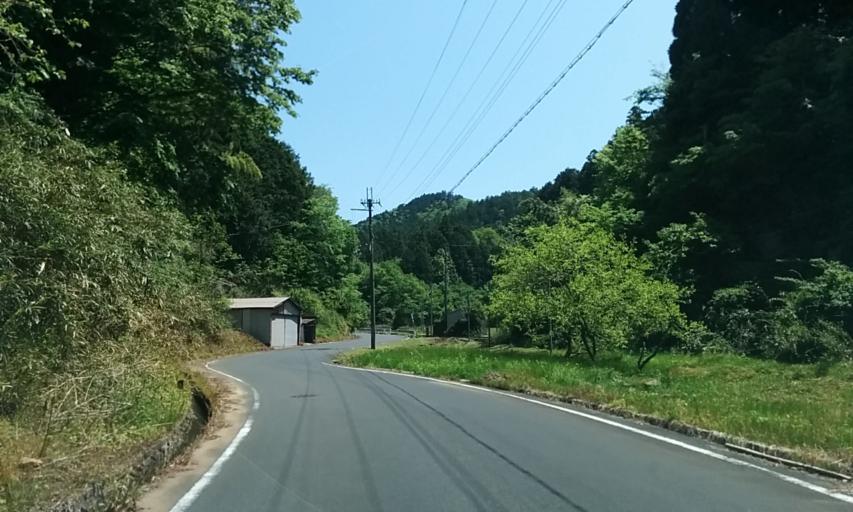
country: JP
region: Kyoto
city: Ayabe
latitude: 35.3842
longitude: 135.1843
